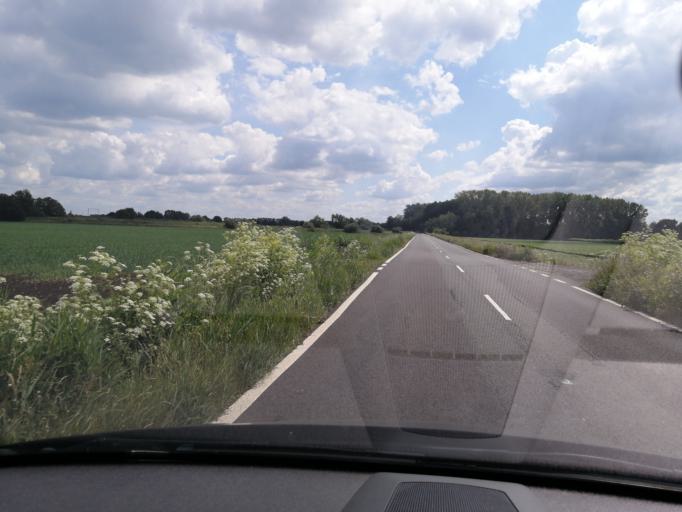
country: GB
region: England
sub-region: Cambridgeshire
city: Yaxley
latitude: 52.4849
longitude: -0.2430
